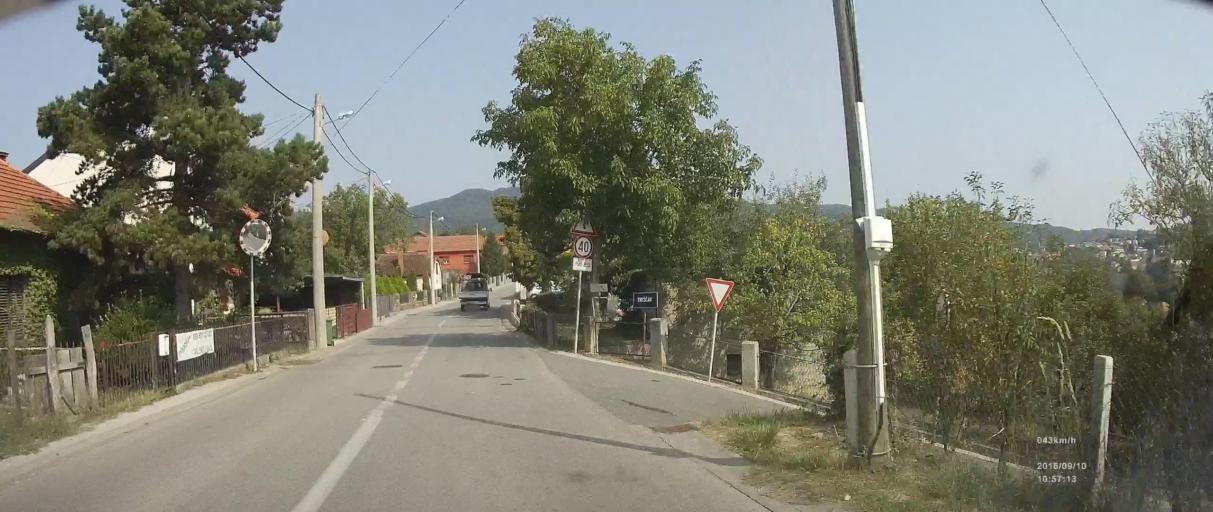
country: HR
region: Grad Zagreb
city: Zagreb
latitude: 45.8407
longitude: 15.9360
